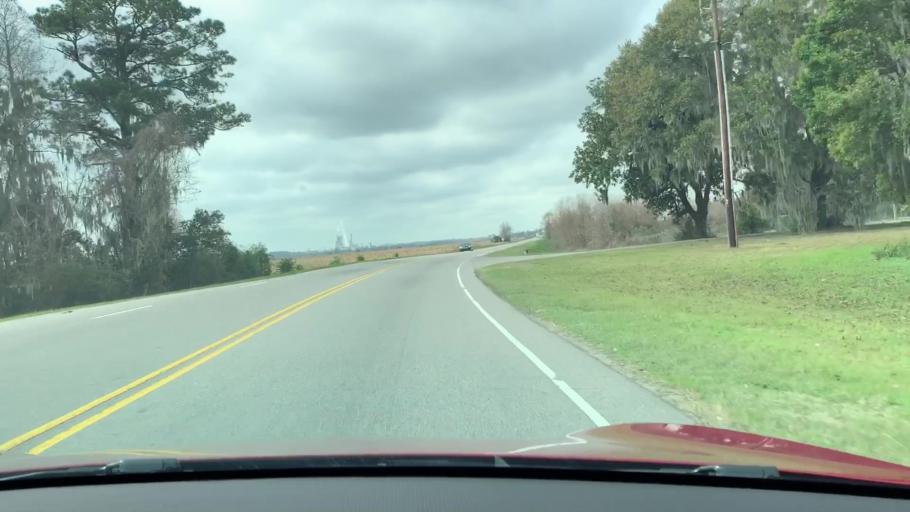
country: US
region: Georgia
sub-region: Chatham County
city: Port Wentworth
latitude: 32.1661
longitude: -81.1158
